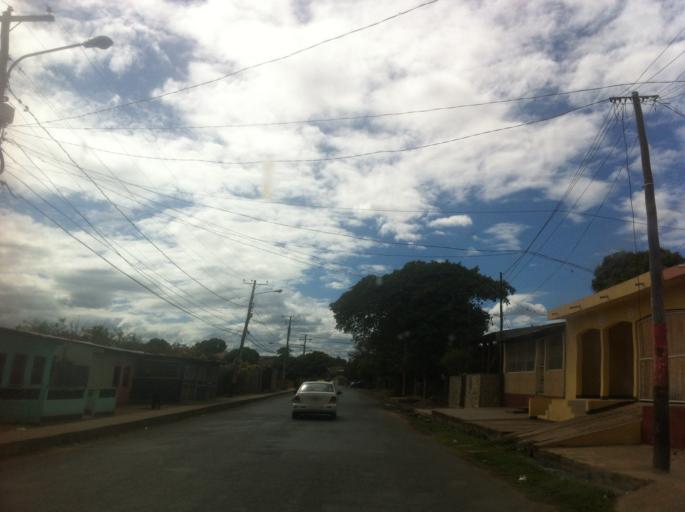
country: NI
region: Granada
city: Granada
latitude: 11.9406
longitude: -85.9506
